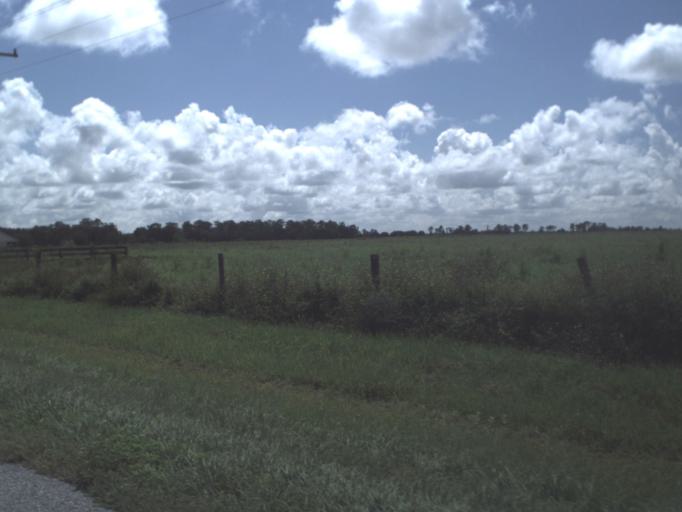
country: US
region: Florida
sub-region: DeSoto County
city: Arcadia
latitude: 27.3122
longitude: -82.1042
